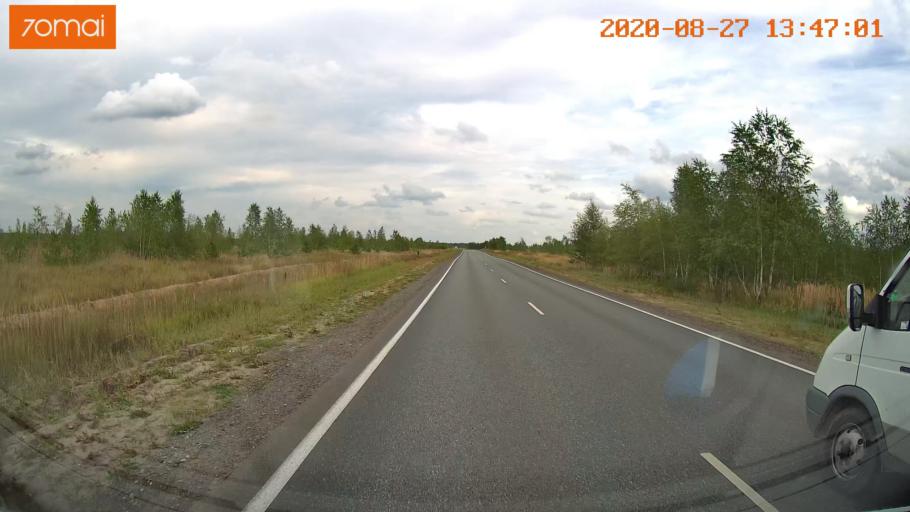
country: RU
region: Rjazan
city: Solotcha
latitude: 54.8631
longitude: 39.9748
